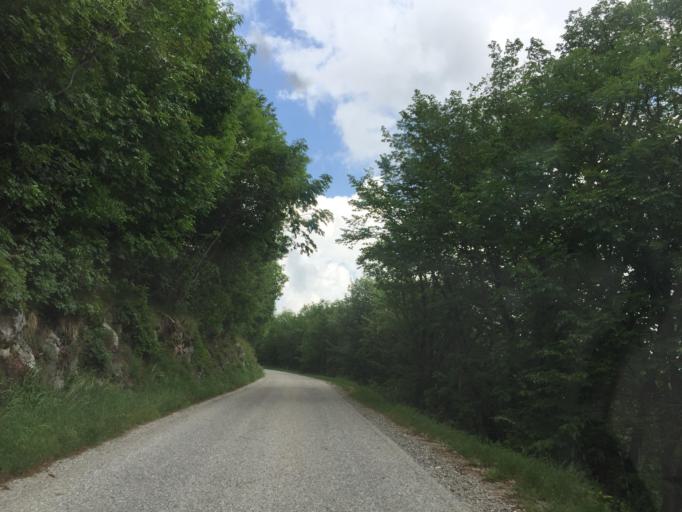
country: SI
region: Nova Gorica
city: Sempas
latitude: 46.0205
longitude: 13.7417
